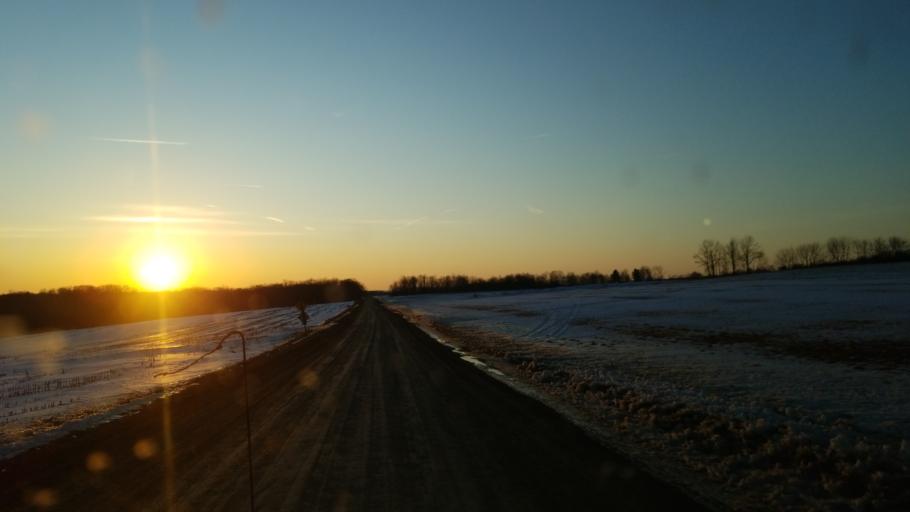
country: US
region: Pennsylvania
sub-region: Tioga County
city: Westfield
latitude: 42.0128
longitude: -77.6605
